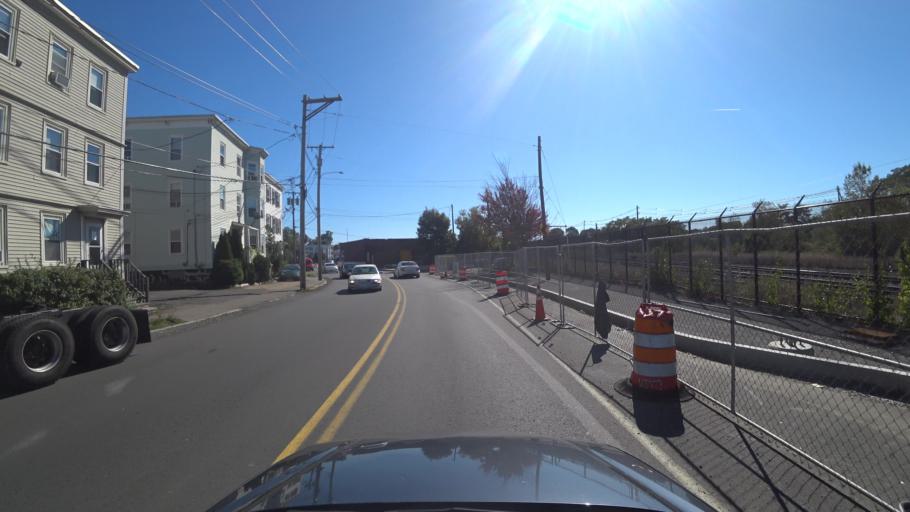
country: US
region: Massachusetts
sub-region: Essex County
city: Salem
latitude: 42.5113
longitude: -70.8966
